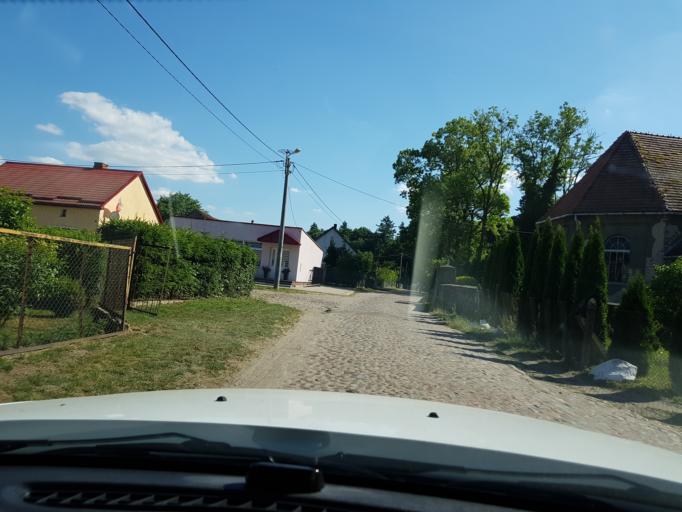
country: PL
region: West Pomeranian Voivodeship
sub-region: Powiat bialogardzki
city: Karlino
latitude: 53.9343
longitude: 15.8273
